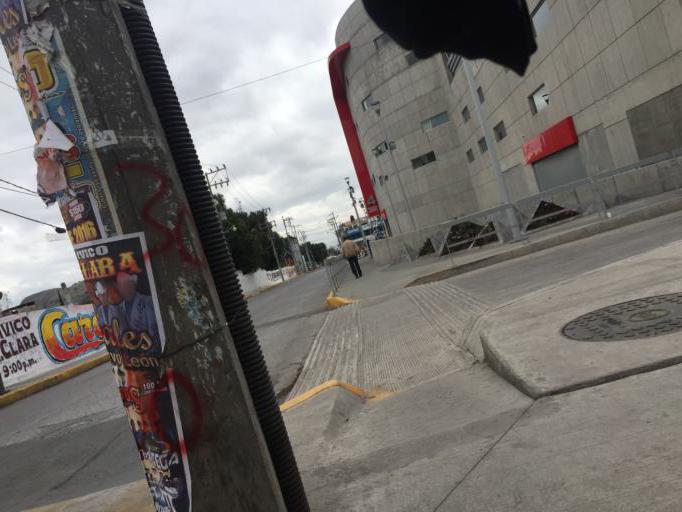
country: MX
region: Mexico
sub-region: Tlalnepantla de Baz
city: Puerto Escondido (Tepeolulco Puerto Escondido)
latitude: 19.5568
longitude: -99.0808
